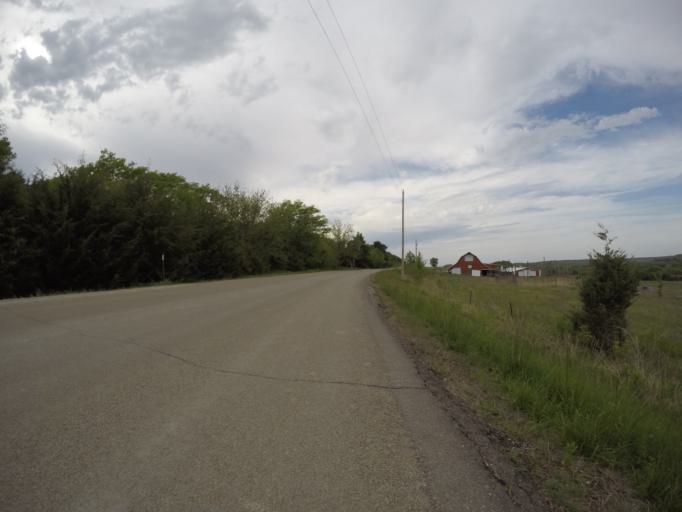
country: US
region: Kansas
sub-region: Riley County
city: Ogden
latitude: 39.0553
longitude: -96.6485
